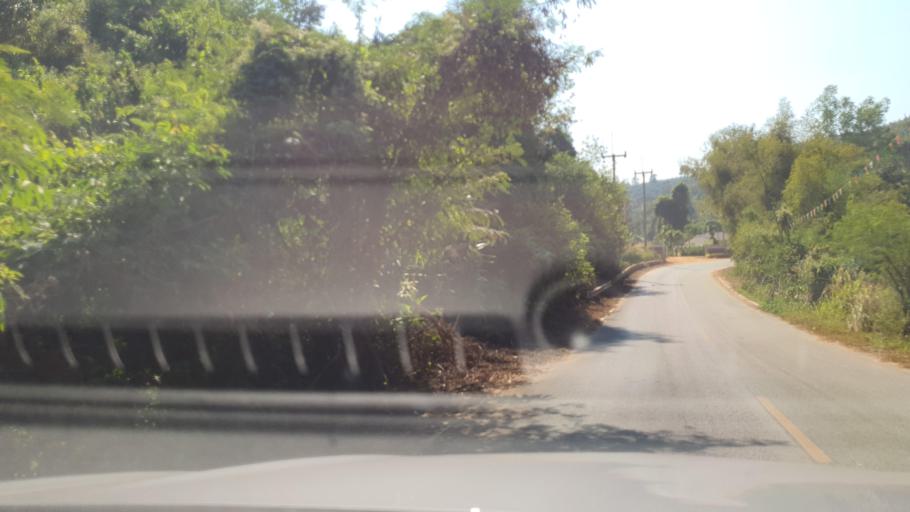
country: TH
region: Nan
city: Pua
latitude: 19.1655
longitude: 100.9098
